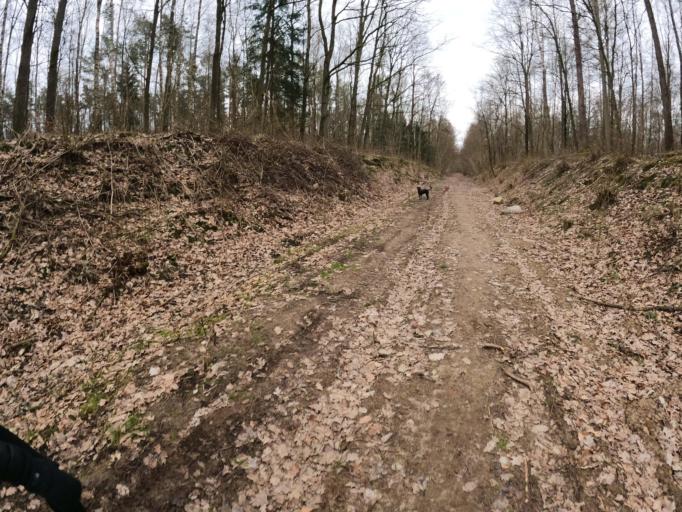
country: PL
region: West Pomeranian Voivodeship
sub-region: Powiat kamienski
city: Golczewo
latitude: 53.8138
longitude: 14.9925
